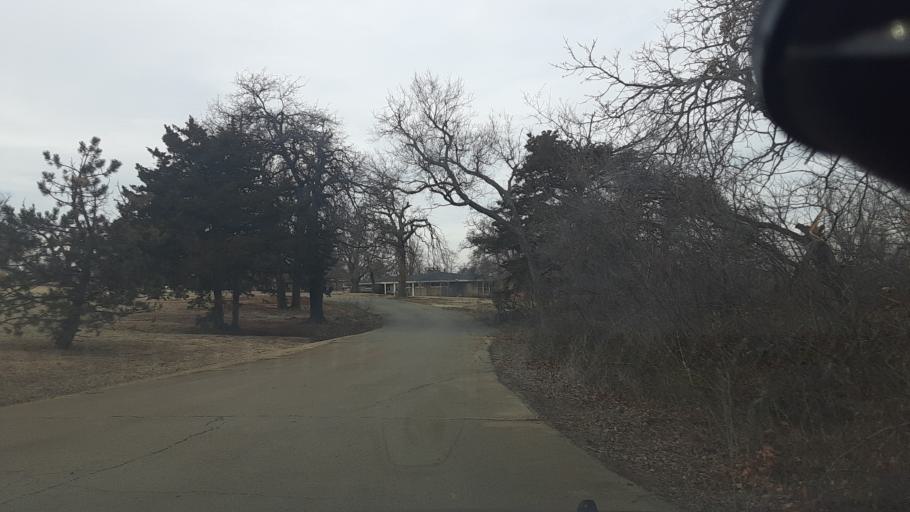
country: US
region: Oklahoma
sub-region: Logan County
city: Guthrie
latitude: 35.8837
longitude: -97.4127
